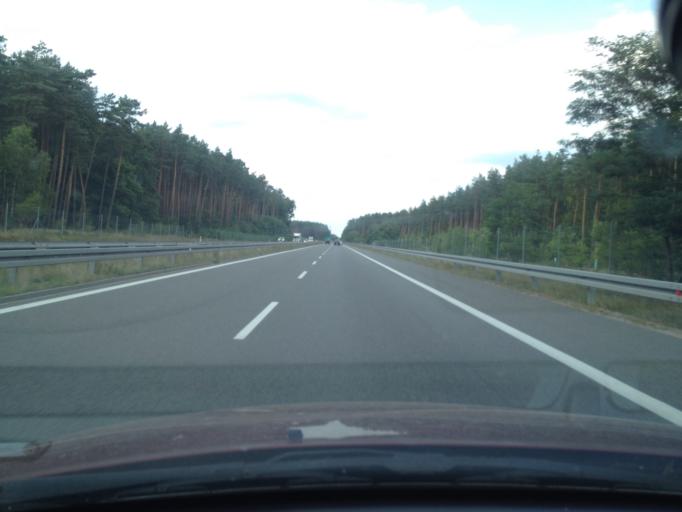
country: PL
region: West Pomeranian Voivodeship
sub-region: Powiat goleniowski
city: Goleniow
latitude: 53.5993
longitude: 14.8247
